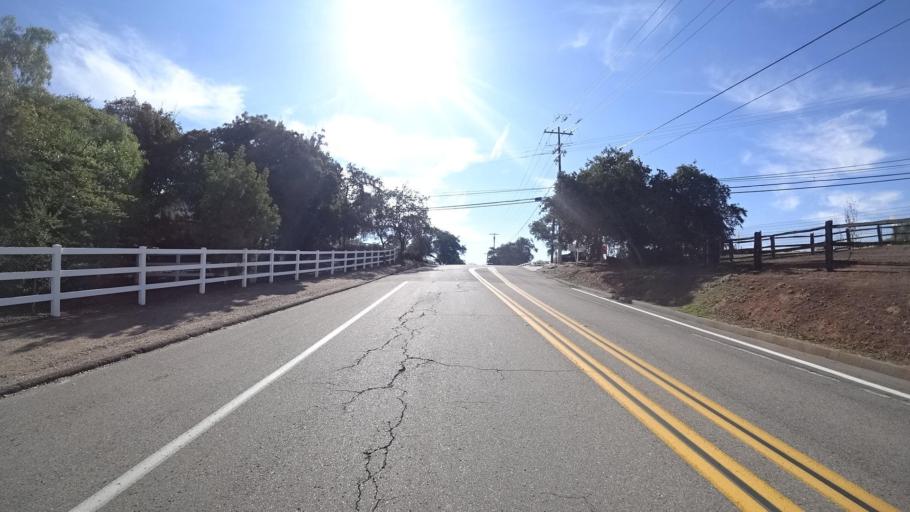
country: US
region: California
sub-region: San Diego County
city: Alpine
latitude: 32.8194
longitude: -116.7844
